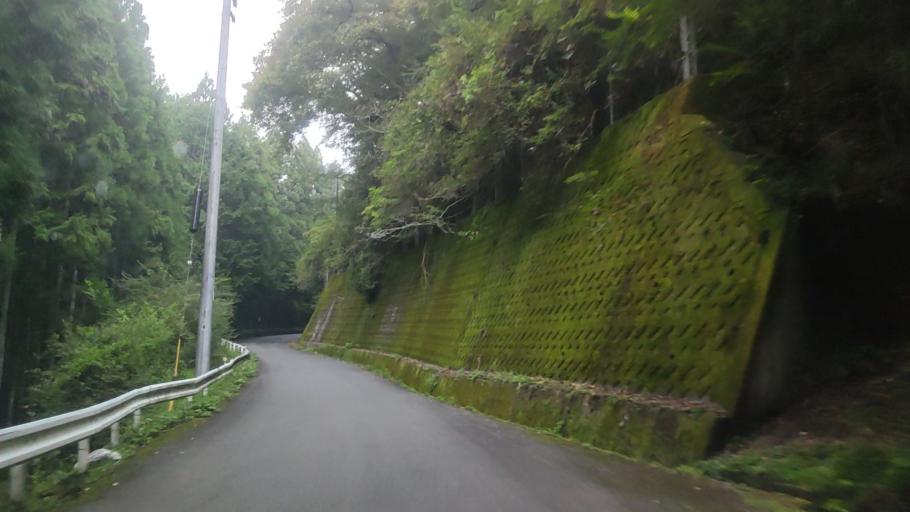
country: JP
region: Wakayama
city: Hashimoto
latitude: 34.2828
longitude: 135.6282
